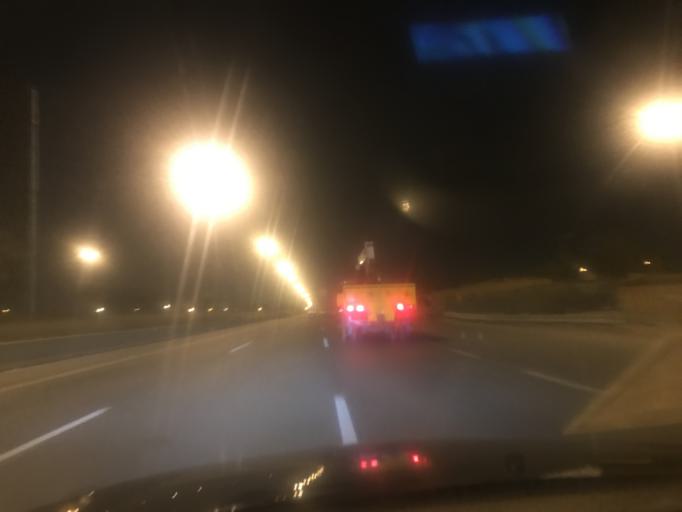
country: SA
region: Ar Riyad
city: Riyadh
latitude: 24.7965
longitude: 46.5648
